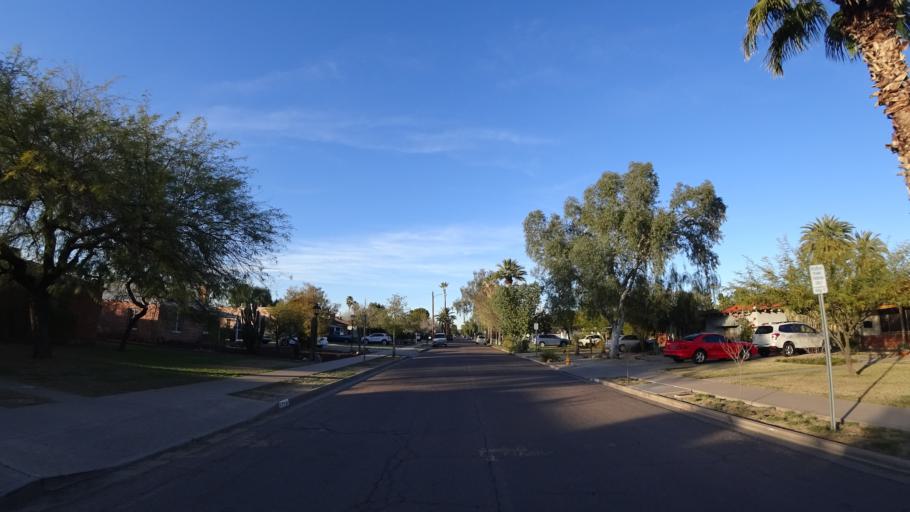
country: US
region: Arizona
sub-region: Maricopa County
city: Phoenix
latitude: 33.4674
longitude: -112.0926
